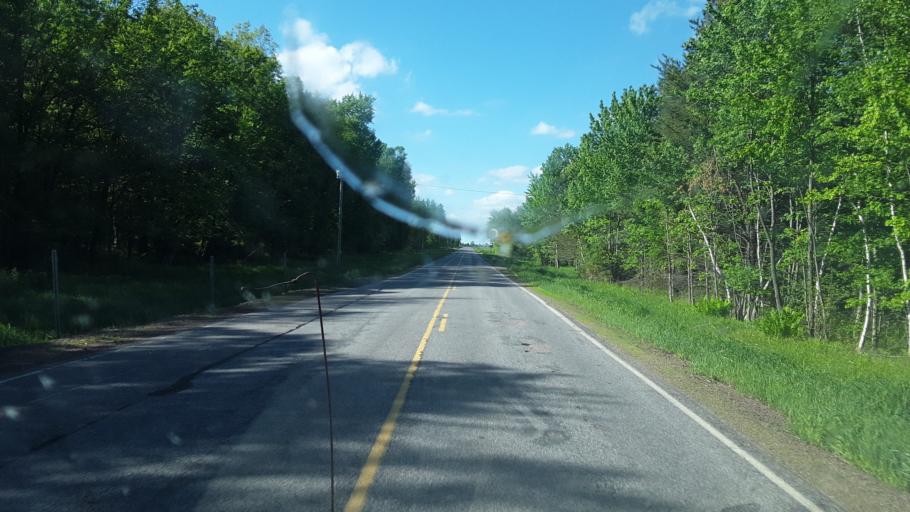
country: US
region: Wisconsin
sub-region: Wood County
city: Marshfield
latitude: 44.4099
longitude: -90.1603
